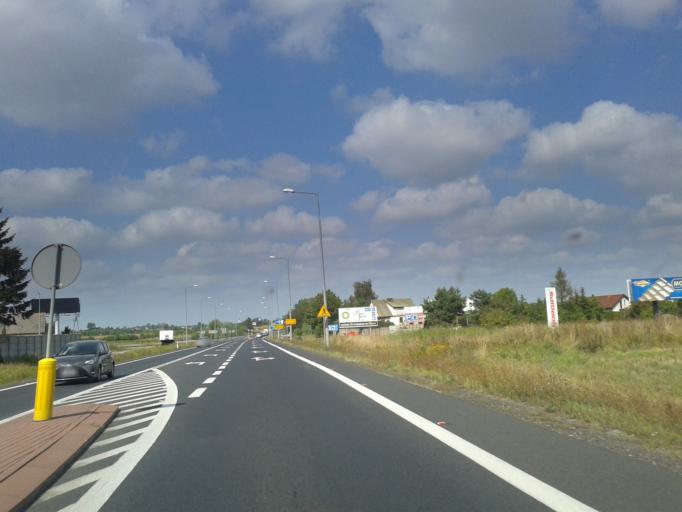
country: PL
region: Greater Poland Voivodeship
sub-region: Powiat poznanski
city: Zlotniki
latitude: 52.5511
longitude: 16.8377
